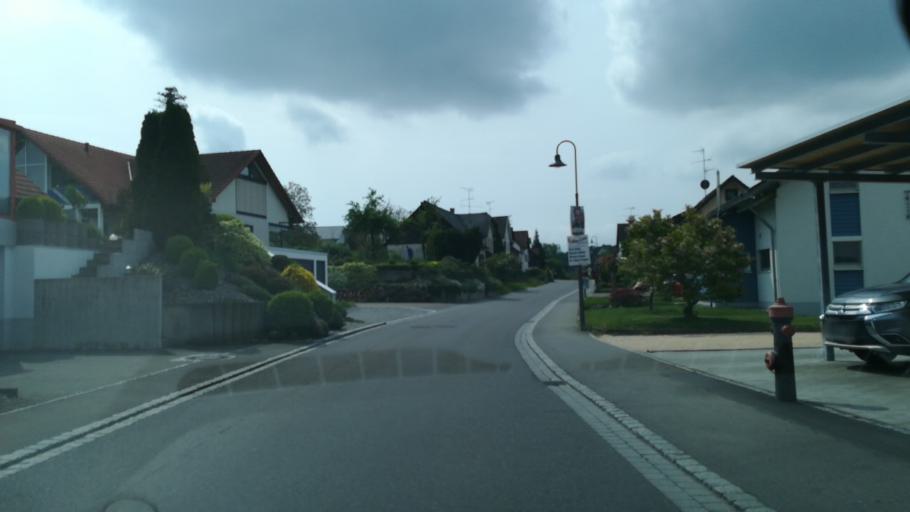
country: DE
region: Baden-Wuerttemberg
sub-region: Freiburg Region
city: Volkertshausen
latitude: 47.7850
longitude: 8.8781
